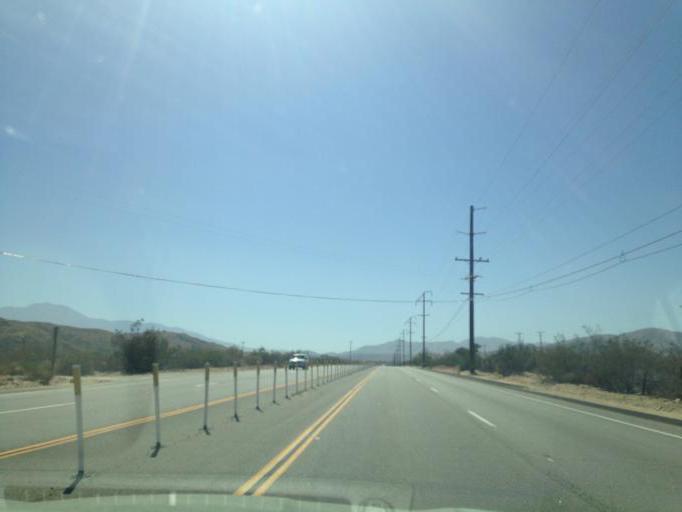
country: US
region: California
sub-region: San Bernardino County
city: Morongo Valley
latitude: 34.0909
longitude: -116.5171
